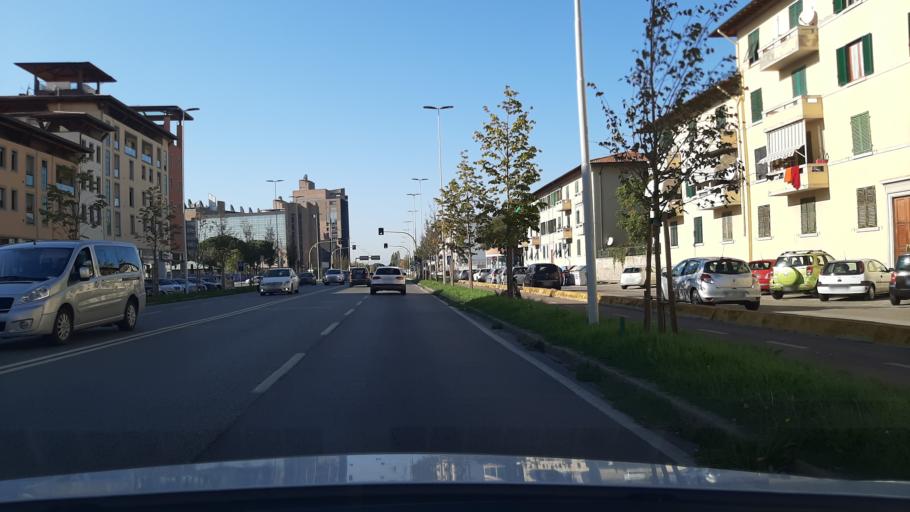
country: IT
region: Tuscany
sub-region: Province of Florence
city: Florence
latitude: 43.7943
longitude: 11.2314
